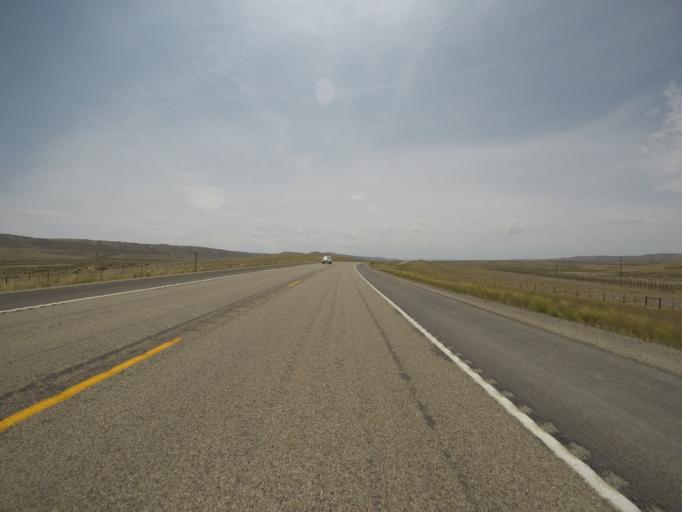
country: US
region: Wyoming
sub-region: Lincoln County
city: Kemmerer
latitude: 41.7156
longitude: -110.5660
